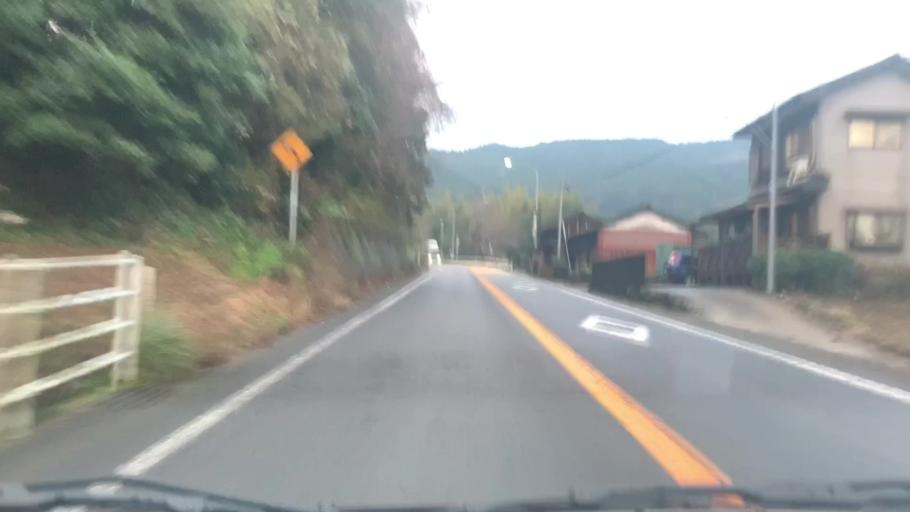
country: JP
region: Saga Prefecture
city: Ureshinomachi-shimojuku
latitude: 33.0741
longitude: 129.9618
